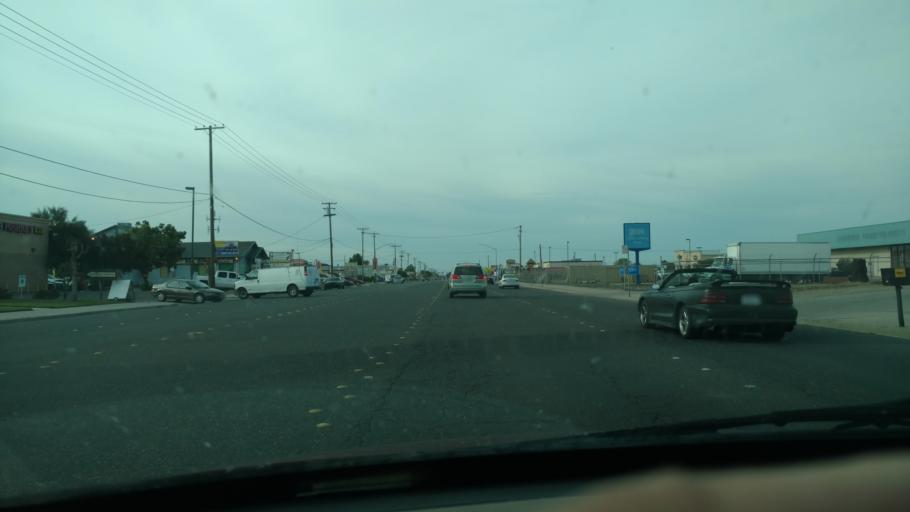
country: US
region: California
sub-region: Stanislaus County
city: Bret Harte
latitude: 37.5988
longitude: -120.9935
